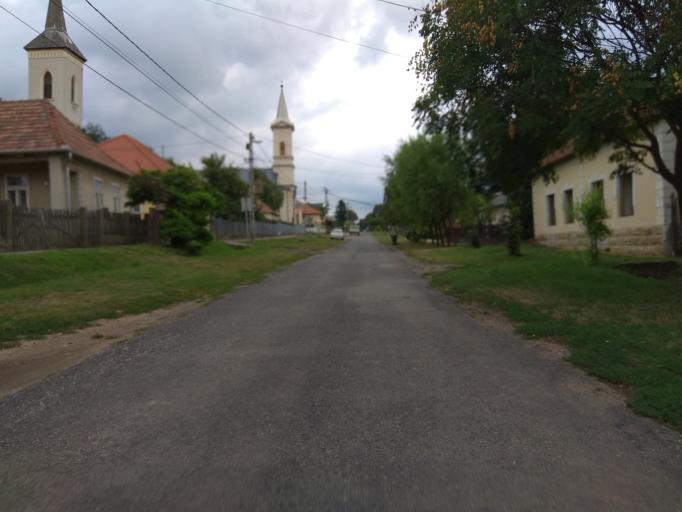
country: HU
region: Borsod-Abauj-Zemplen
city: Gesztely
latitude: 48.1373
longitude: 21.0048
